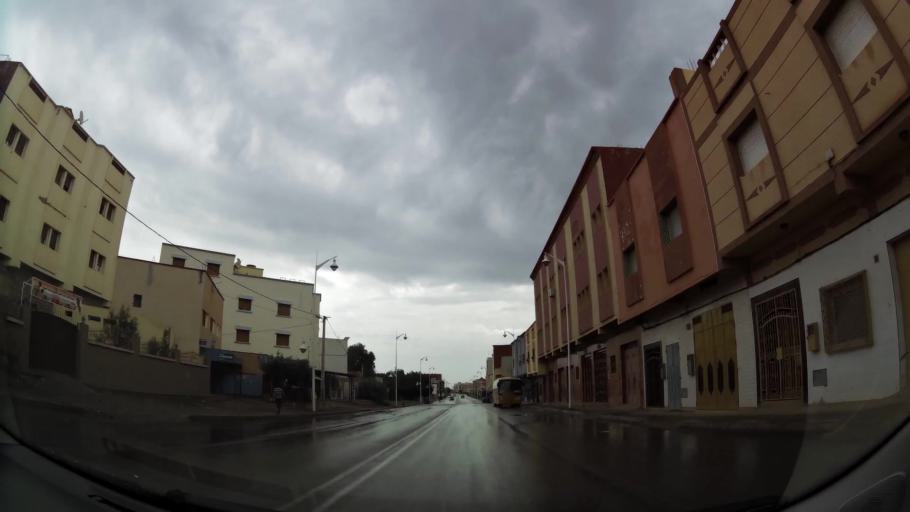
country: MA
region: Oriental
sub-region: Nador
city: Nador
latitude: 35.1529
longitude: -2.9870
